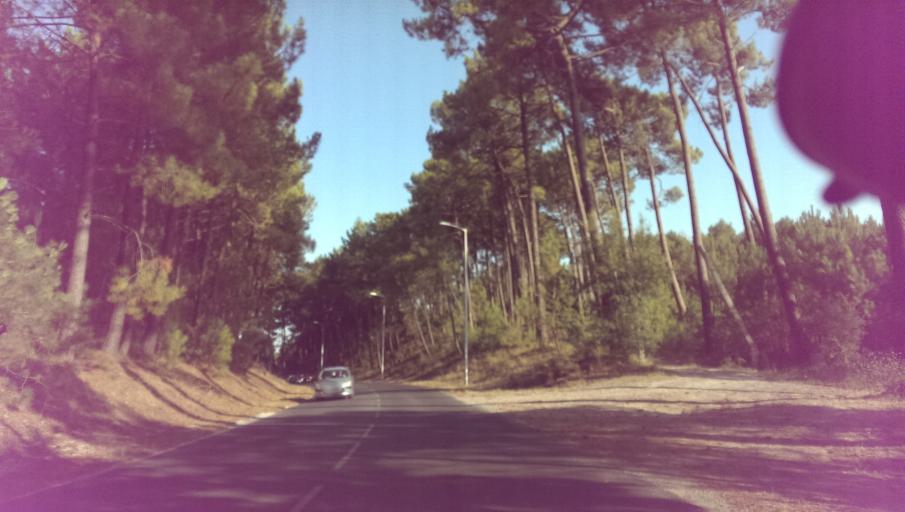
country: FR
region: Aquitaine
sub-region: Departement des Landes
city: Mimizan
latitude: 44.2047
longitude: -1.2382
